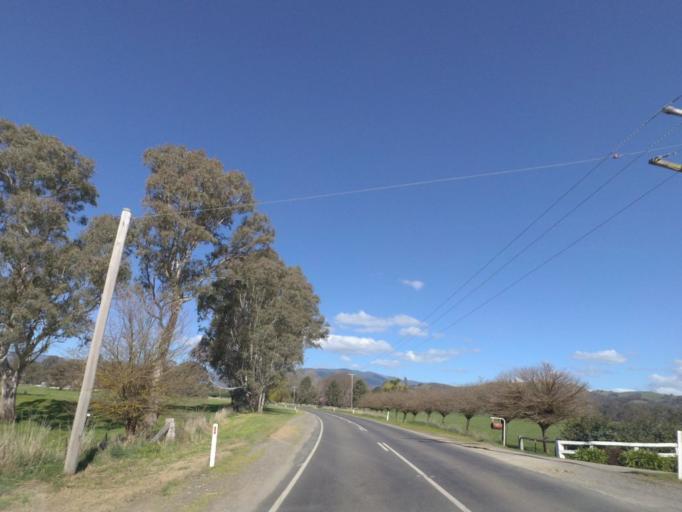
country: AU
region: Victoria
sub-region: Murrindindi
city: Alexandra
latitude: -37.2416
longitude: 145.7699
